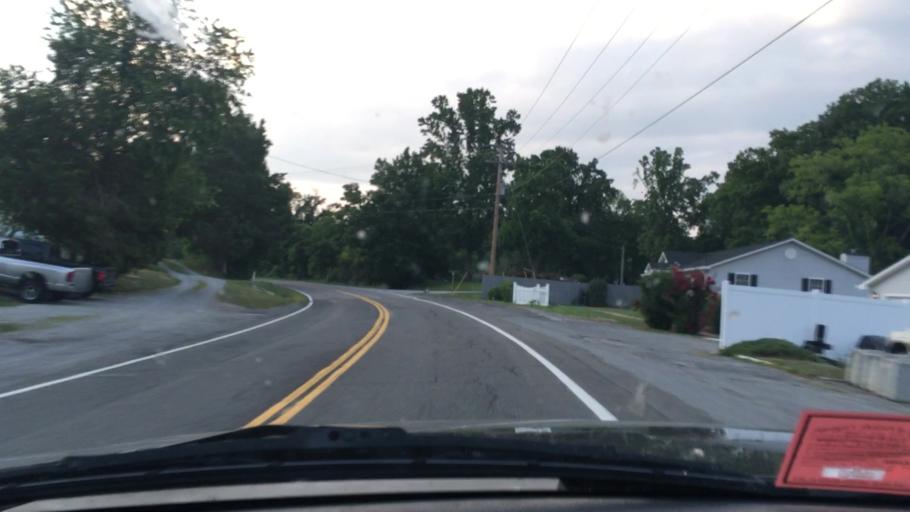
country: US
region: Virginia
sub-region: Pulaski County
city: Dublin
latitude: 37.0466
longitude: -80.7108
